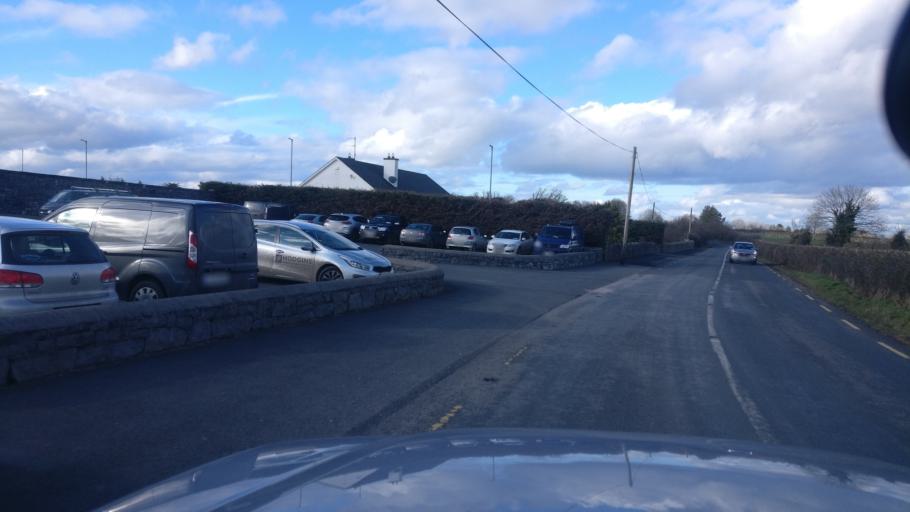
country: IE
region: Connaught
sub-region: County Galway
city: Loughrea
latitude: 53.1749
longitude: -8.3944
